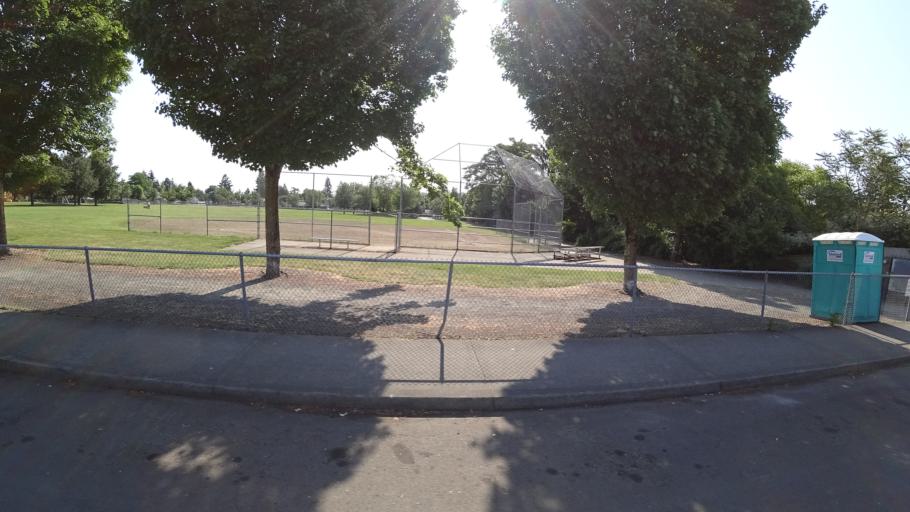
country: US
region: Oregon
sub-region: Multnomah County
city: Lents
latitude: 45.4620
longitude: -122.5945
